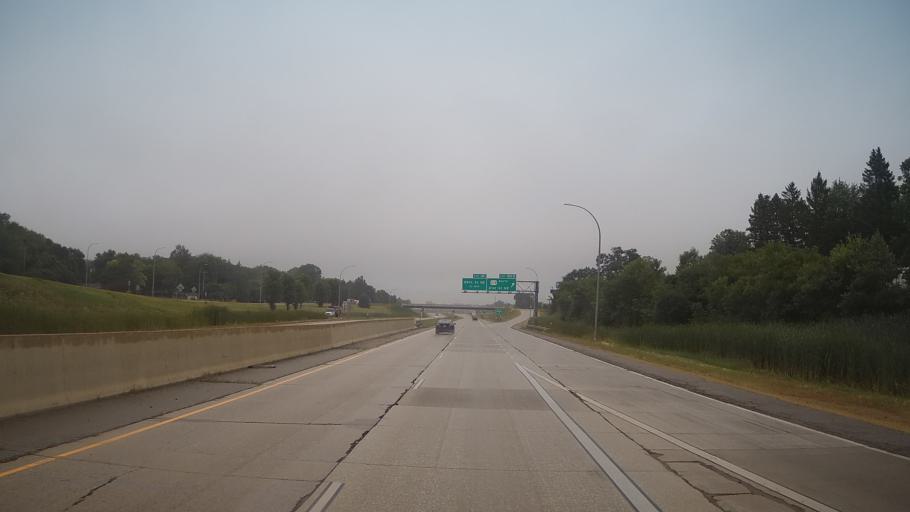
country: US
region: Minnesota
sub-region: Mower County
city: Austin
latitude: 43.6742
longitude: -92.9449
